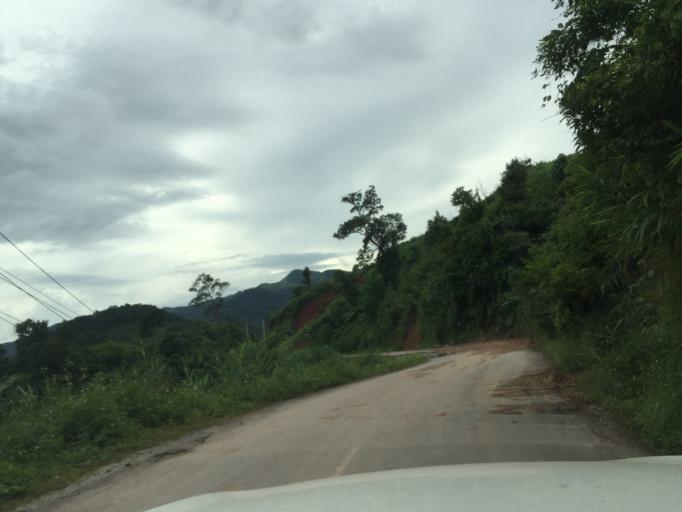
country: LA
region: Oudomxai
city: Muang La
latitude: 21.2360
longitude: 102.0707
